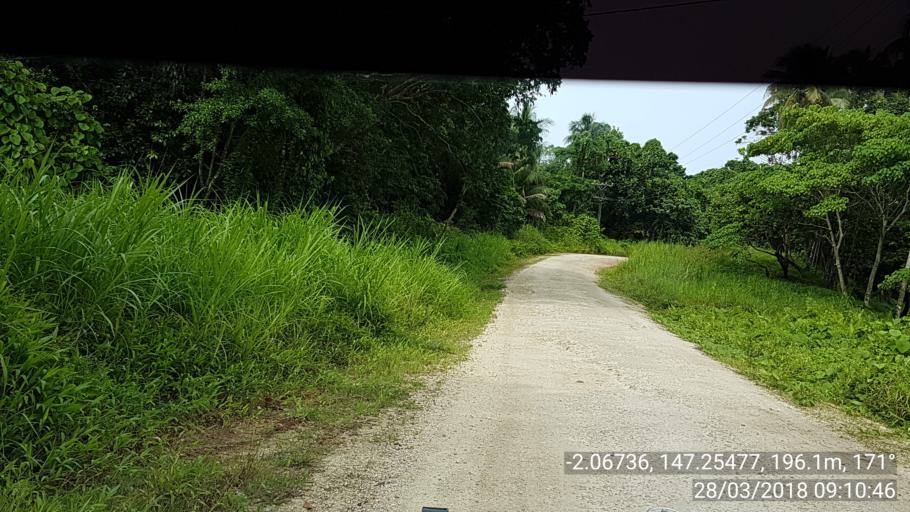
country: PG
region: Manus
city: Lorengau
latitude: -2.0673
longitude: 147.2548
